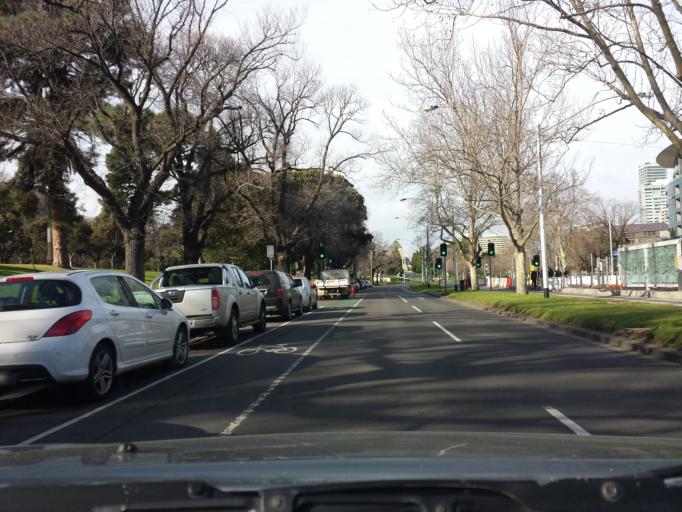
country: AU
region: Victoria
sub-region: Melbourne
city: Southbank
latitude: -37.8243
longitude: 144.9708
